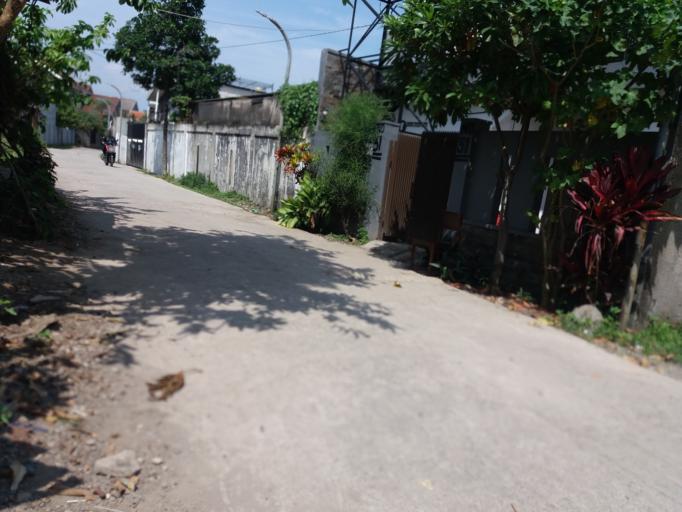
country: ID
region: West Java
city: Bandung
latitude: -6.9196
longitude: 107.6645
